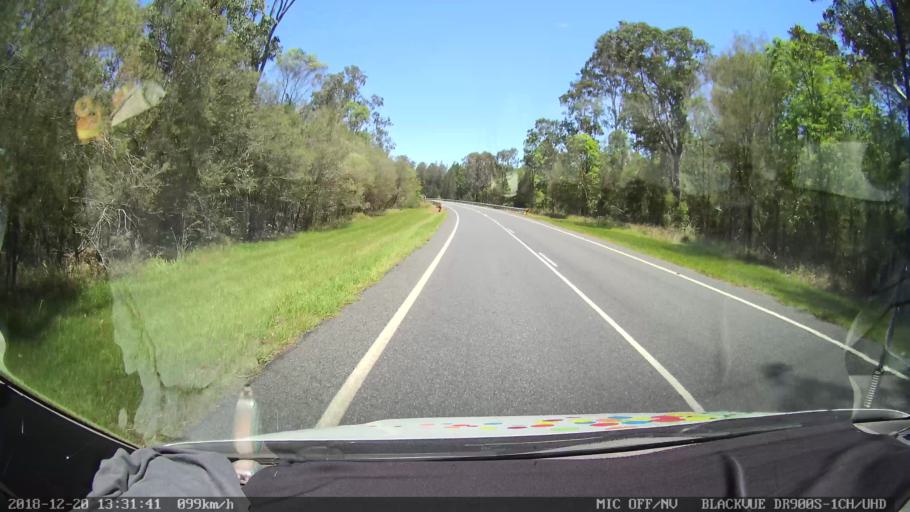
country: AU
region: New South Wales
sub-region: Clarence Valley
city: Gordon
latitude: -29.2215
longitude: 152.9879
